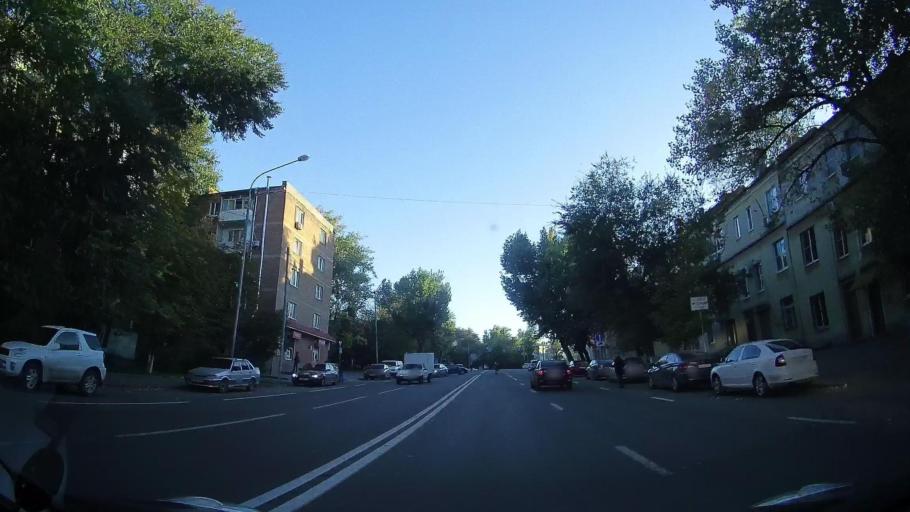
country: RU
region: Rostov
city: Rostov-na-Donu
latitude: 47.2417
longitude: 39.7017
